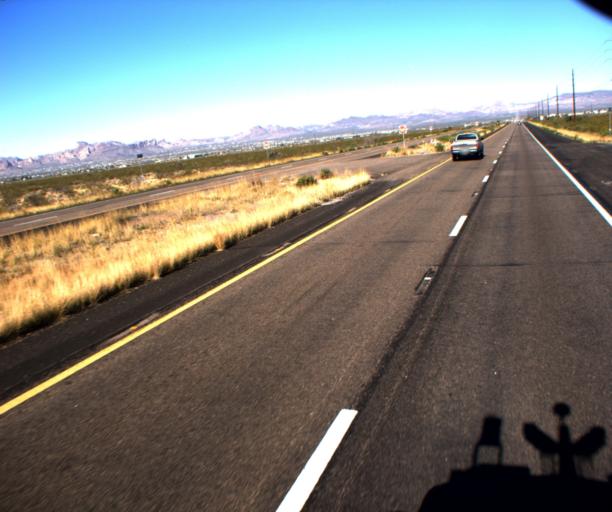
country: US
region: Arizona
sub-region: Mohave County
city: Golden Valley
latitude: 35.2224
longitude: -114.2217
